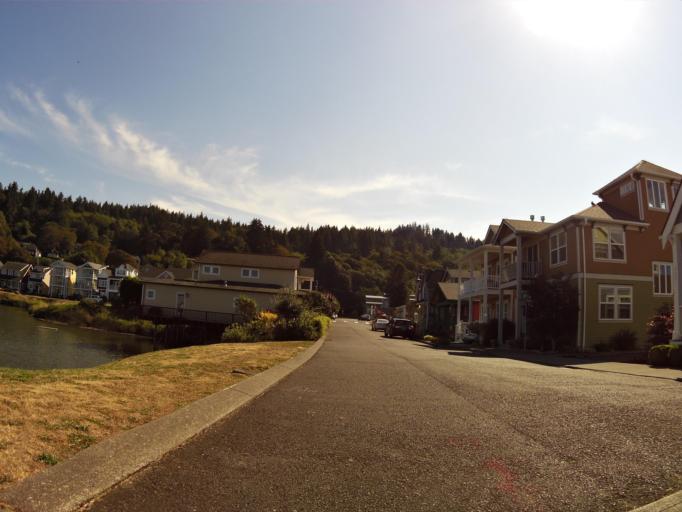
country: US
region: Oregon
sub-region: Clatsop County
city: Astoria
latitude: 46.1905
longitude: -123.8158
